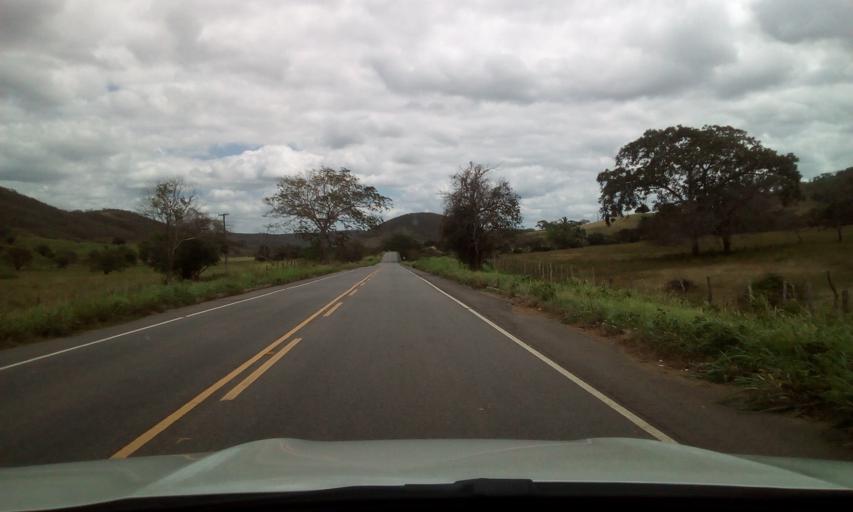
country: BR
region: Paraiba
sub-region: Serra Redonda
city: Alagoa Grande
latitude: -7.1291
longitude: -35.6144
